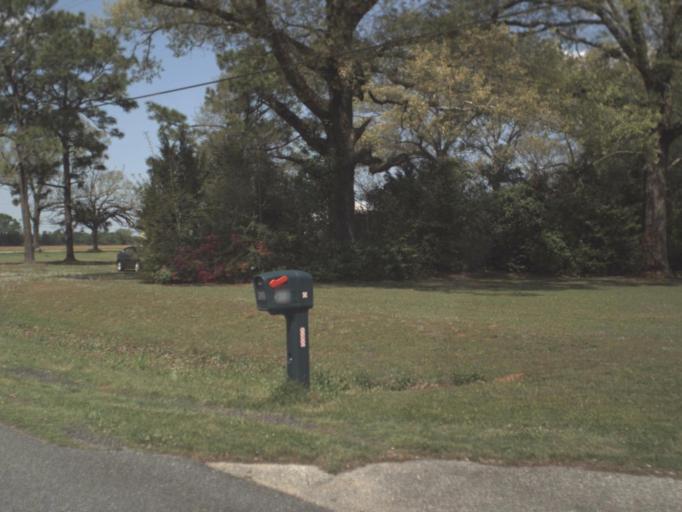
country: US
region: Florida
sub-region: Escambia County
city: Century
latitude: 30.9523
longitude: -87.1204
